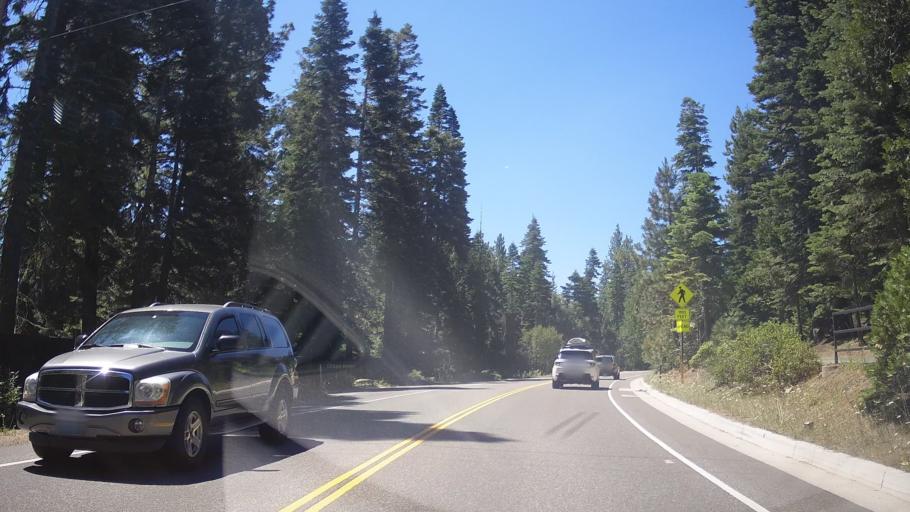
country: US
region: California
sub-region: Placer County
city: Sunnyside-Tahoe City
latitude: 39.1498
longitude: -120.1458
